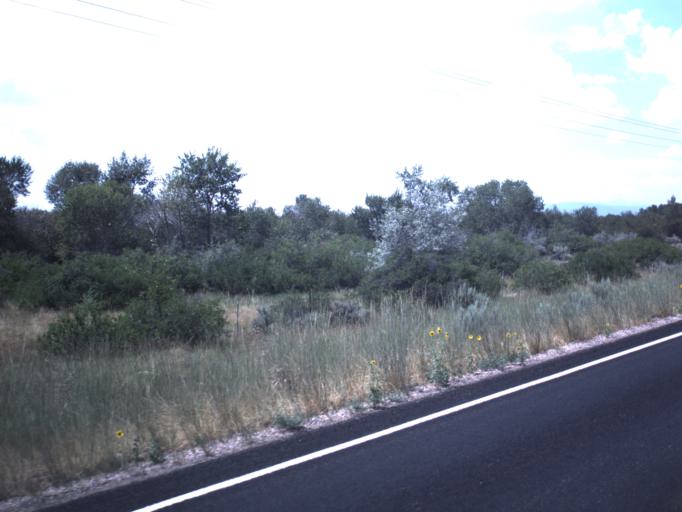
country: US
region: Utah
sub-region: Duchesne County
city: Roosevelt
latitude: 40.4214
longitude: -109.9222
